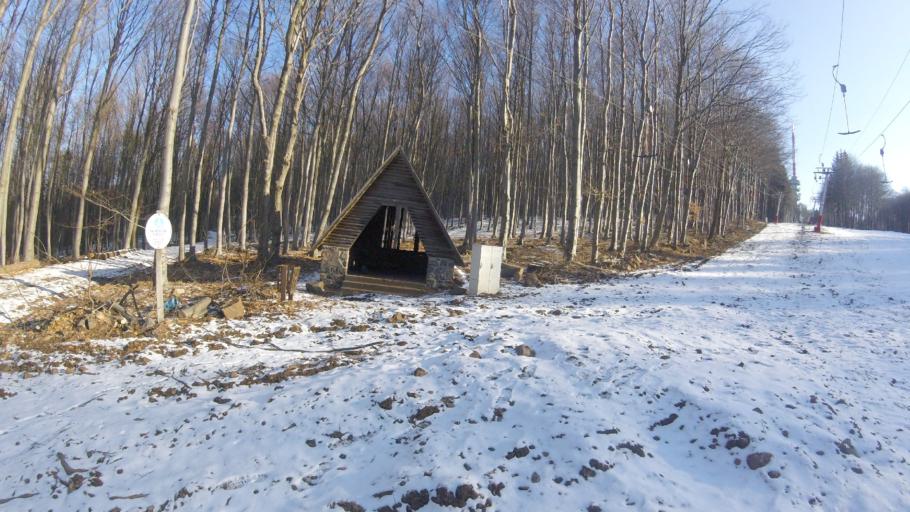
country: HU
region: Heves
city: Paradsasvar
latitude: 47.8722
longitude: 20.0014
